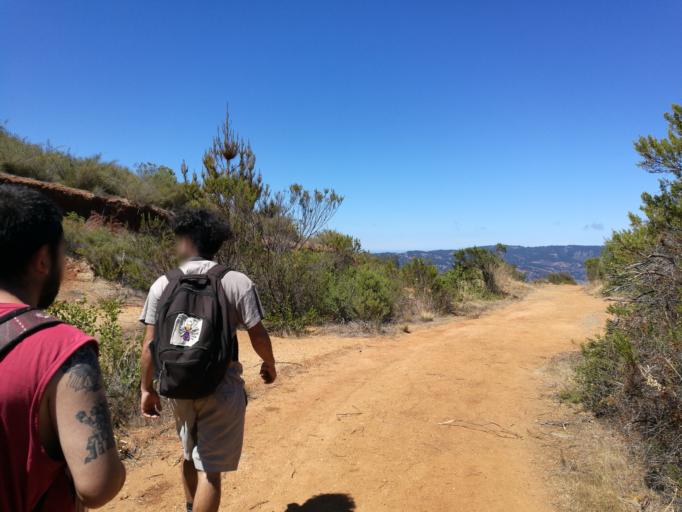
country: CL
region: Valparaiso
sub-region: Provincia de Valparaiso
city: Valparaiso
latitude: -33.0737
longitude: -71.6573
